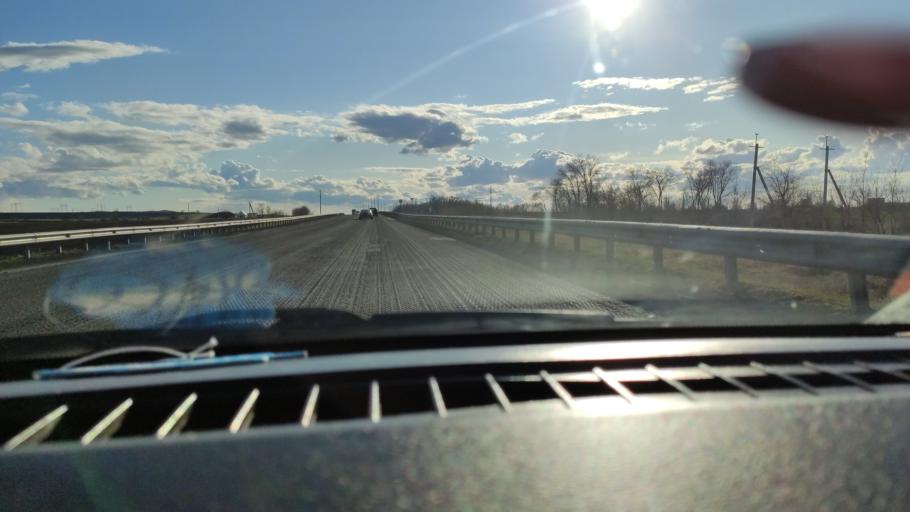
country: RU
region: Saratov
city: Yelshanka
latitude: 51.7916
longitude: 46.1564
